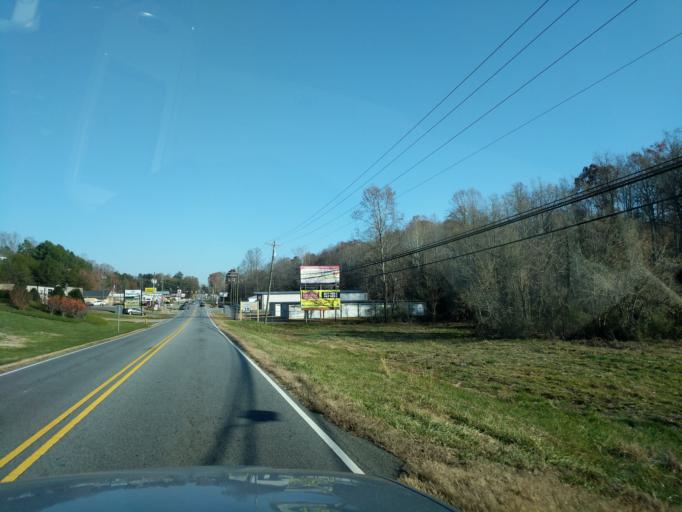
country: US
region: North Carolina
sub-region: Rutherford County
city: Rutherfordton
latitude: 35.3510
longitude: -81.9618
